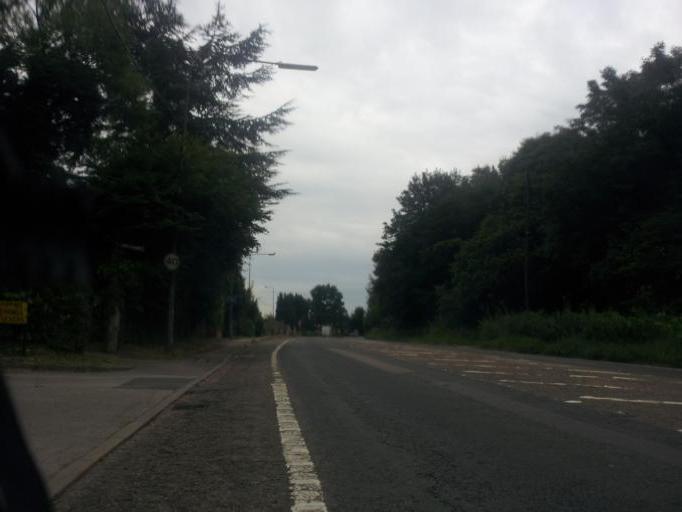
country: GB
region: England
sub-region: Medway
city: Cuxton
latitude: 51.4160
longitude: 0.4489
